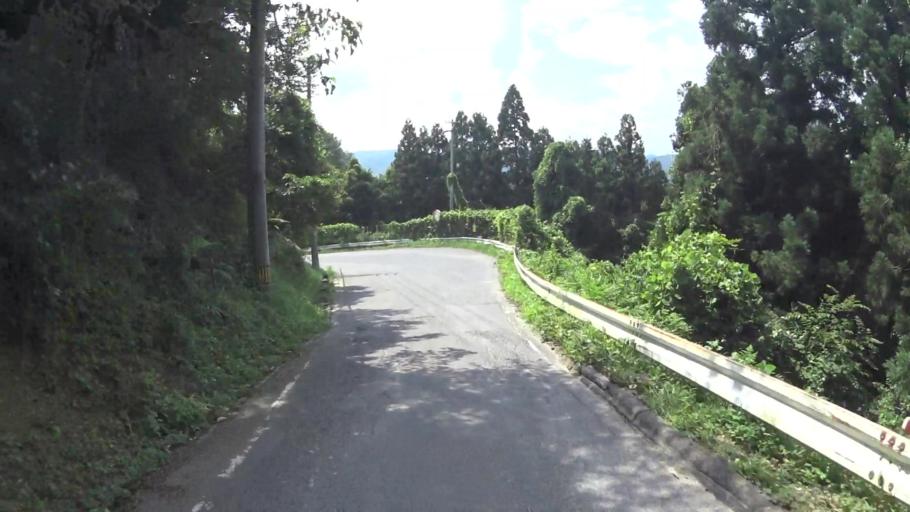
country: JP
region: Mie
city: Ueno-ebisumachi
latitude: 34.8163
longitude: 136.1230
